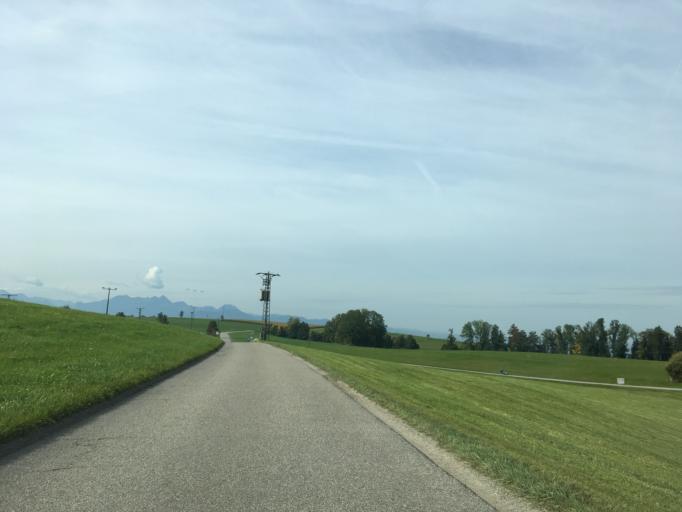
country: DE
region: Bavaria
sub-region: Upper Bavaria
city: Frasdorf
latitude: 47.8386
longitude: 12.2683
